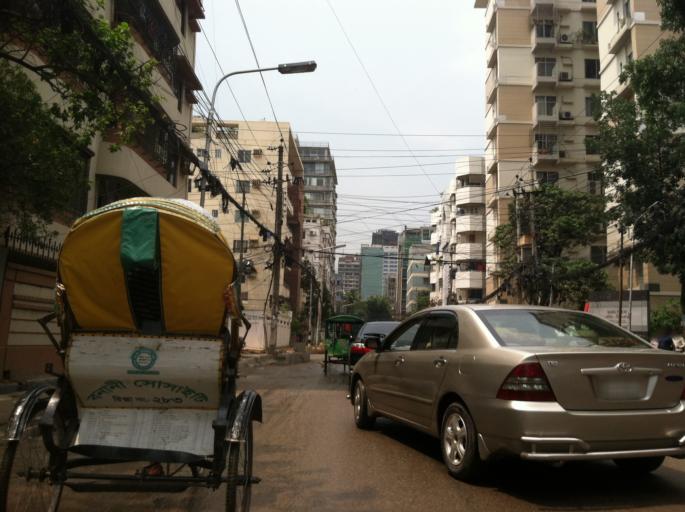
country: BD
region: Dhaka
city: Paltan
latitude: 23.7892
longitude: 90.4037
